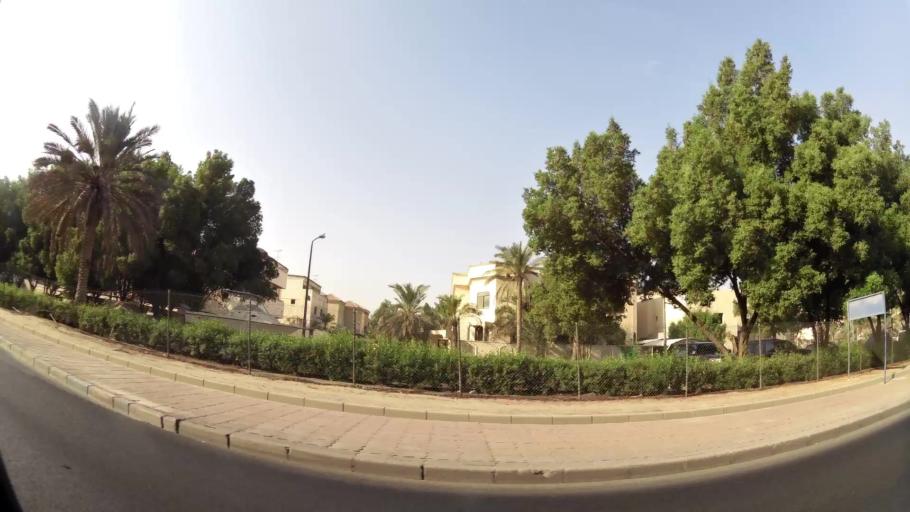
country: KW
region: Muhafazat Hawalli
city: Hawalli
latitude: 29.3505
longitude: 48.0278
